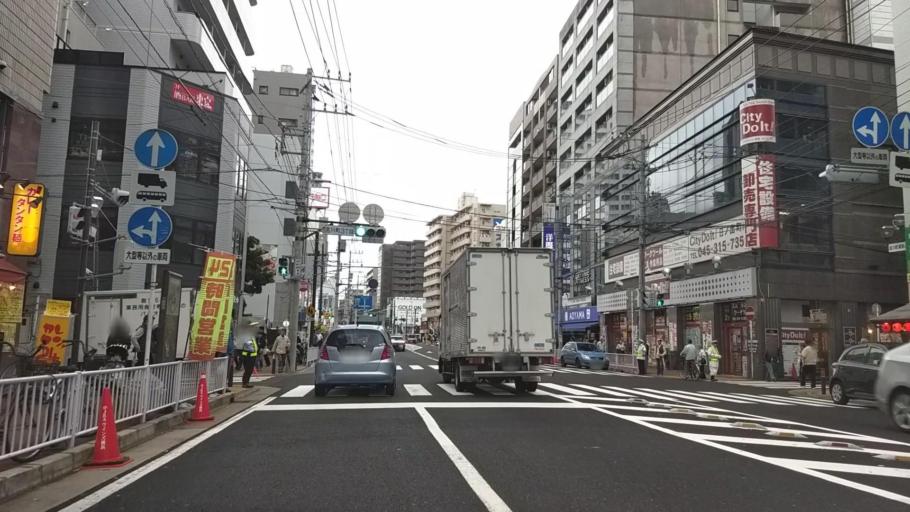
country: JP
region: Kanagawa
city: Yokohama
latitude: 35.4470
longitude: 139.6282
